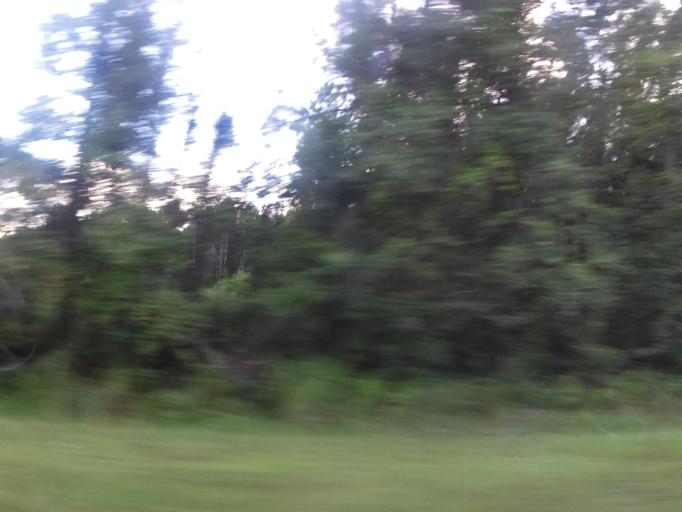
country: US
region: Georgia
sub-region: Camden County
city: St Marys
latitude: 30.7591
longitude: -81.6251
